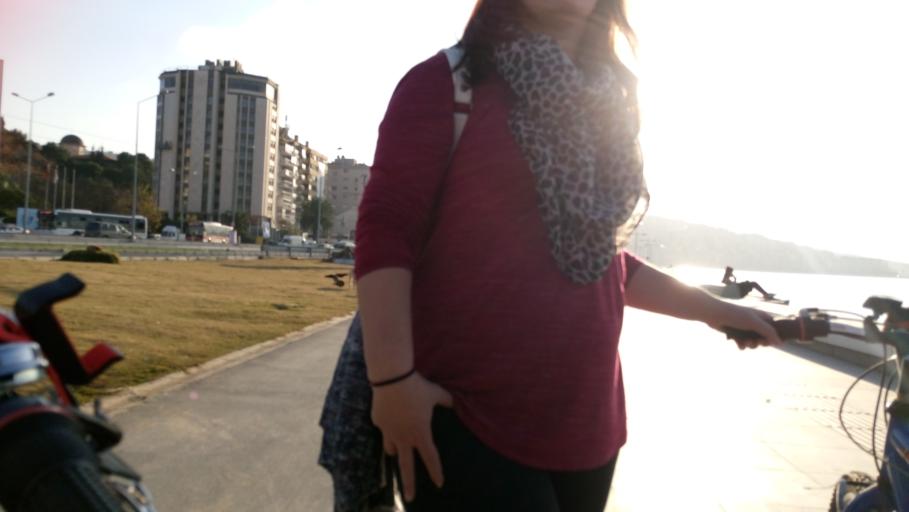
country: TR
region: Izmir
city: Izmir
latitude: 38.4156
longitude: 27.1228
